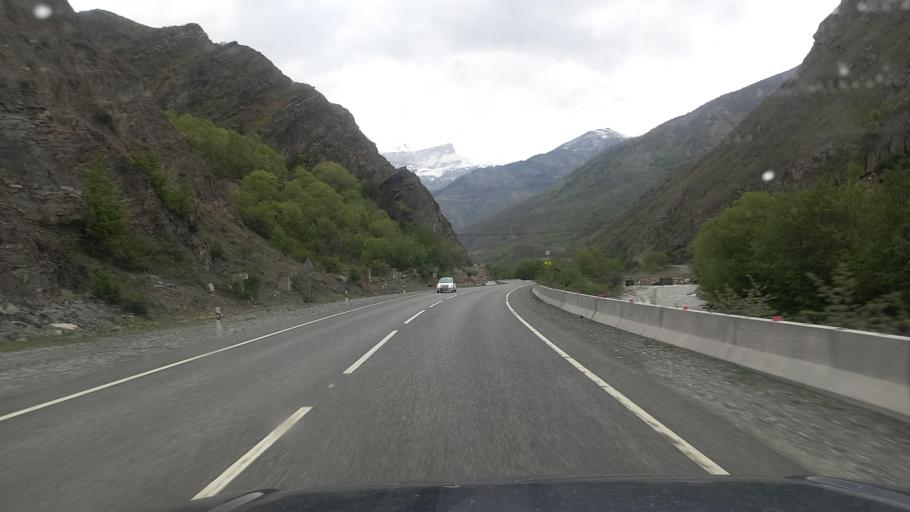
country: RU
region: North Ossetia
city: Mizur
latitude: 42.8577
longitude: 44.1088
